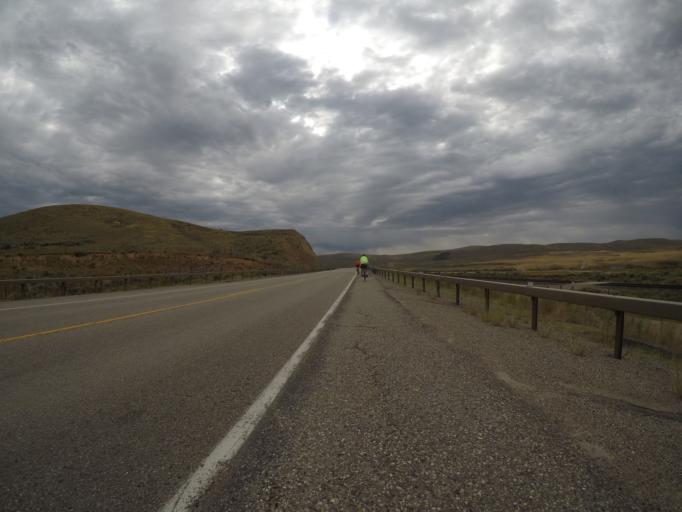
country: US
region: Utah
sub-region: Rich County
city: Randolph
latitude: 41.8222
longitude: -110.8908
